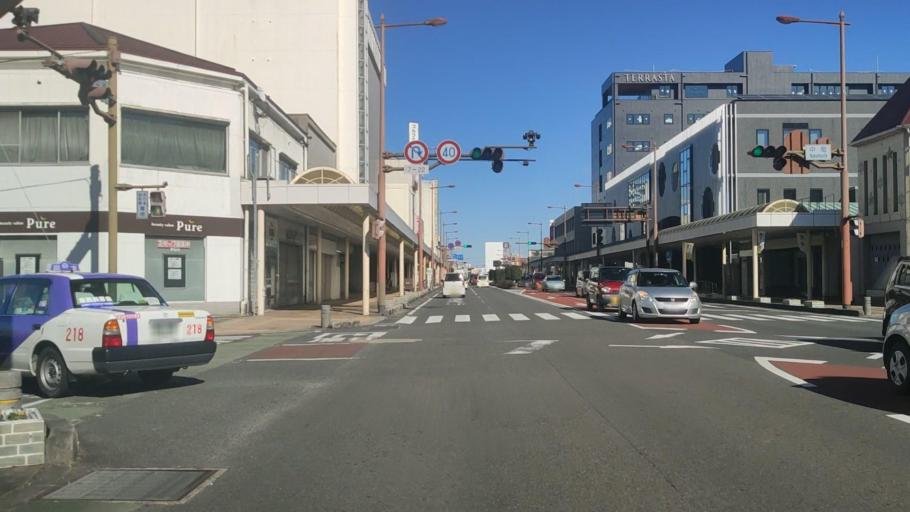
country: JP
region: Miyazaki
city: Miyakonojo
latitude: 31.7252
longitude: 131.0638
